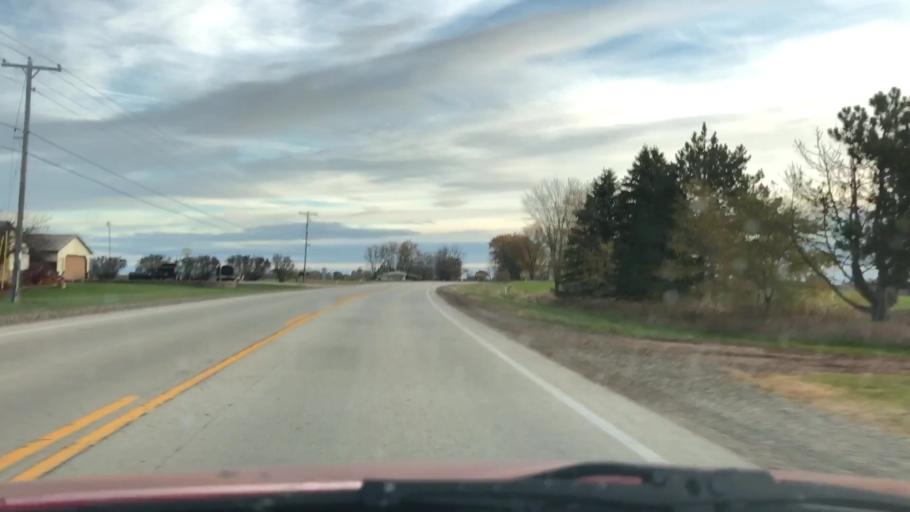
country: US
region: Wisconsin
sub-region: Brown County
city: Oneida
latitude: 44.4195
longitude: -88.2519
